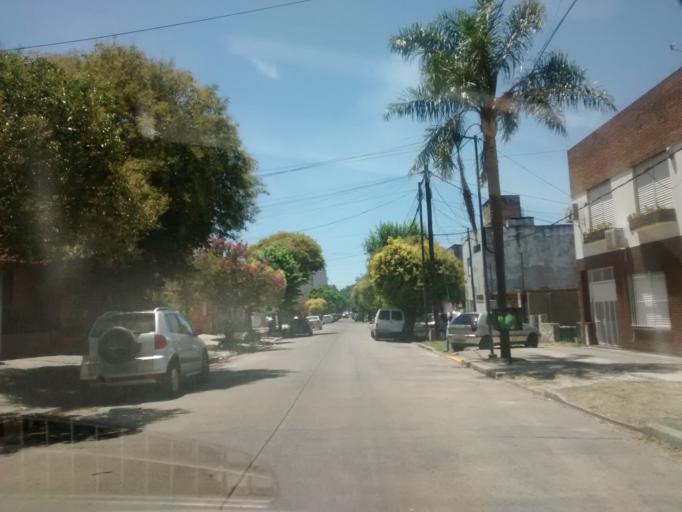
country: AR
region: Buenos Aires
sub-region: Partido de La Plata
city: La Plata
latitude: -34.9482
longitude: -57.9570
